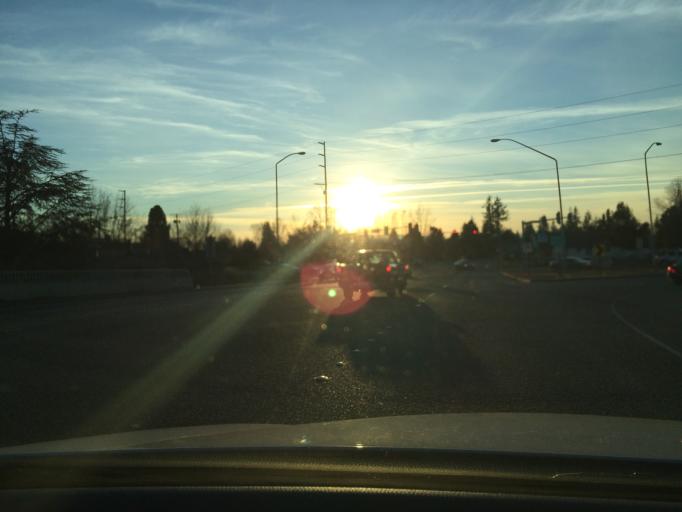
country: US
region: Washington
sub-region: Whatcom County
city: Bellingham
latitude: 48.7710
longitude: -122.4639
